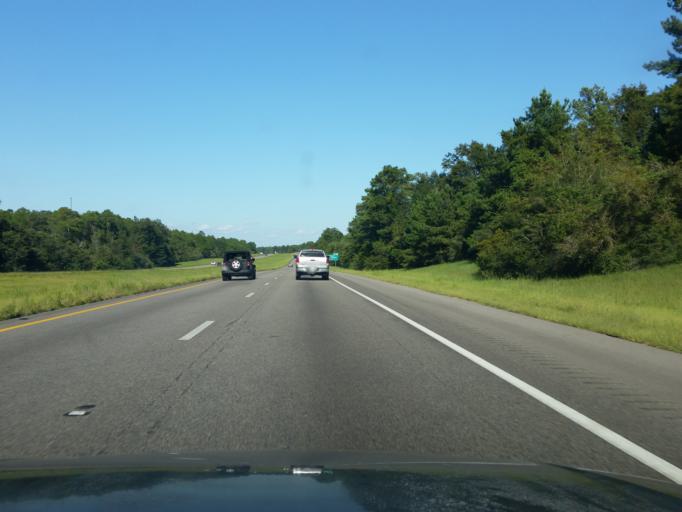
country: US
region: Mississippi
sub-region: Hancock County
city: Diamondhead
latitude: 30.3853
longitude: -89.3351
